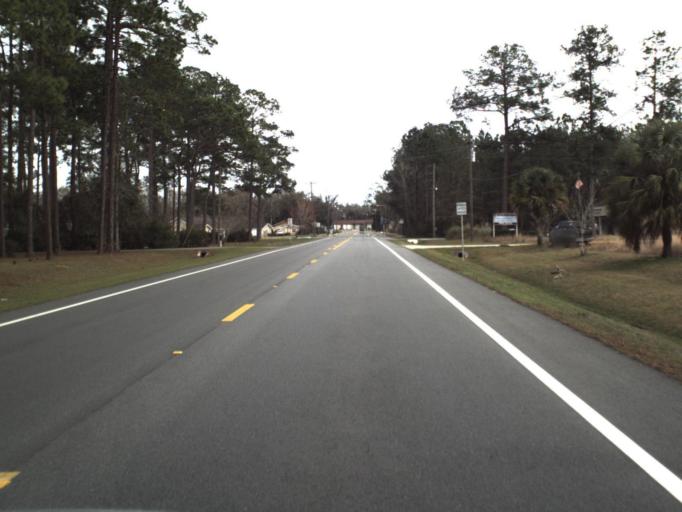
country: US
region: Florida
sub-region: Gulf County
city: Wewahitchka
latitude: 30.1157
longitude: -85.2060
